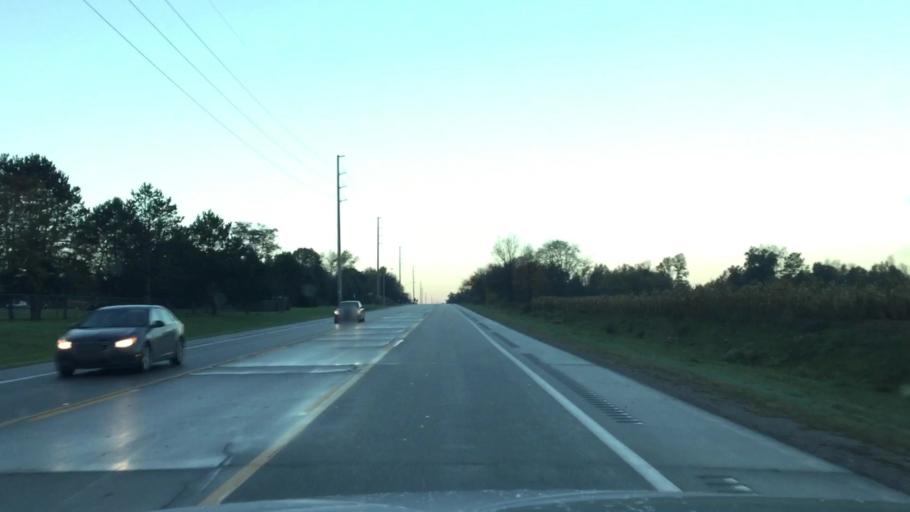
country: US
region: Michigan
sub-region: Livingston County
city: Brighton
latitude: 42.6308
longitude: -83.8218
